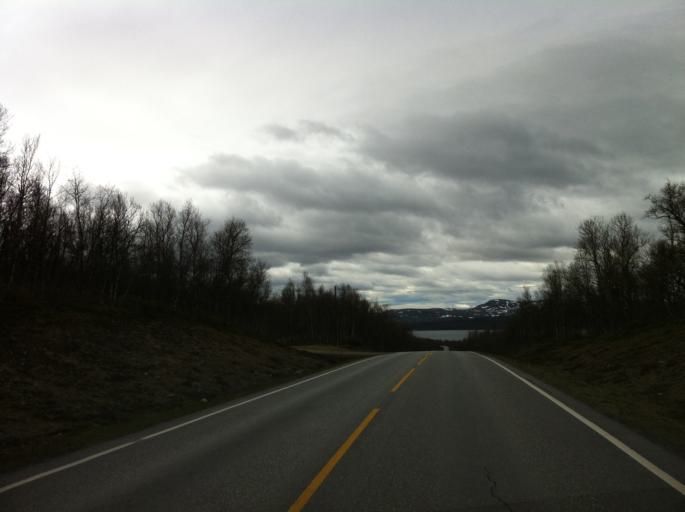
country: NO
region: Sor-Trondelag
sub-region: Tydal
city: Aas
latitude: 62.6389
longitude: 11.8397
